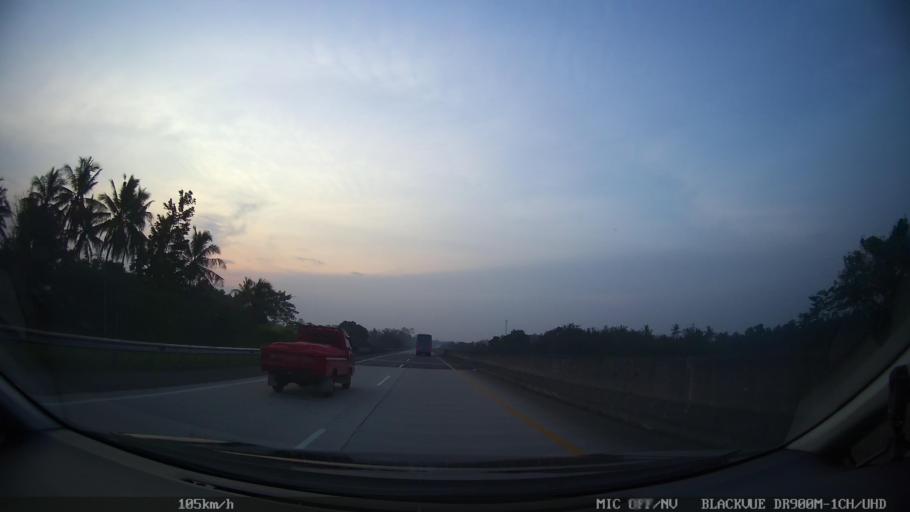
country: ID
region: Lampung
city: Pasuruan
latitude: -5.7131
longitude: 105.6515
